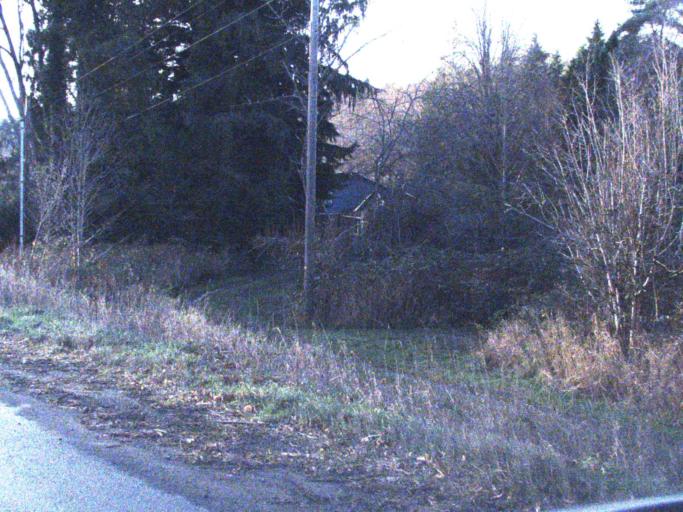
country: US
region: Washington
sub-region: Skagit County
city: Sedro-Woolley
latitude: 48.5299
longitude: -122.1549
